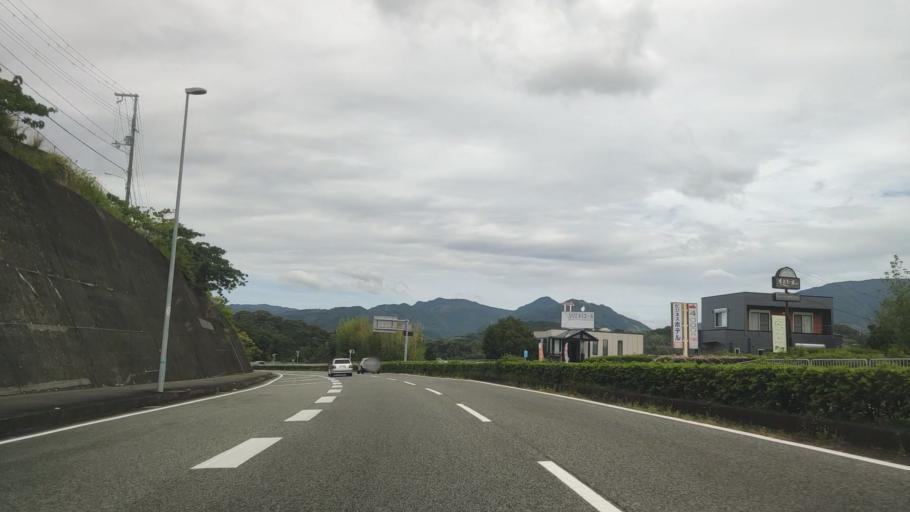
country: JP
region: Wakayama
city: Tanabe
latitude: 33.7340
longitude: 135.4007
